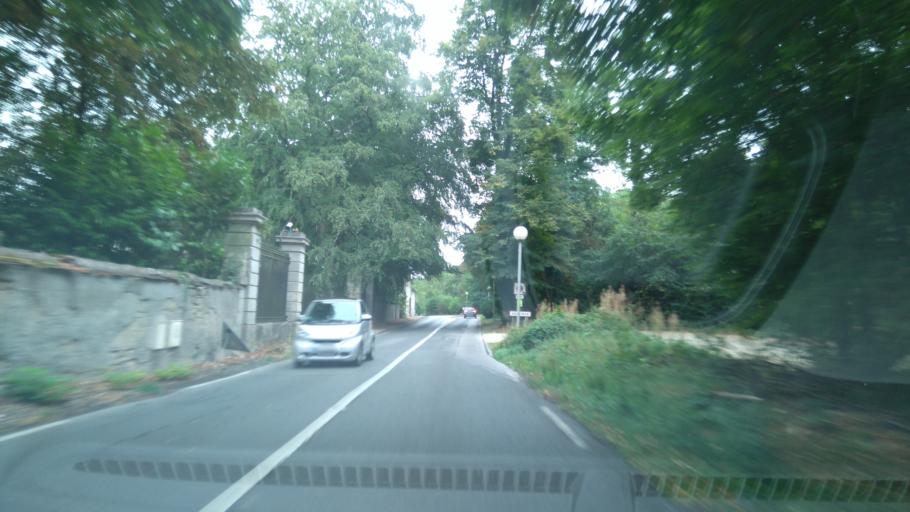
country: FR
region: Picardie
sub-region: Departement de l'Oise
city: Gouvieux
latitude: 49.1874
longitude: 2.4020
